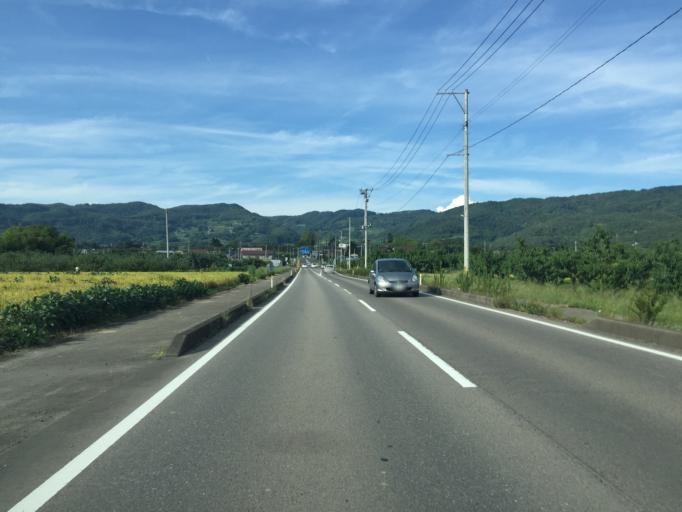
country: JP
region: Fukushima
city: Fukushima-shi
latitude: 37.8246
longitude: 140.4662
